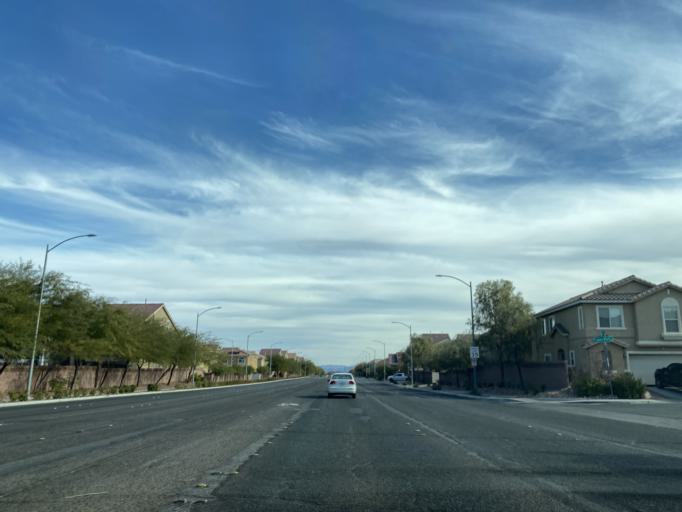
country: US
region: Nevada
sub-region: Clark County
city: Enterprise
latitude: 36.0561
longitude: -115.2332
